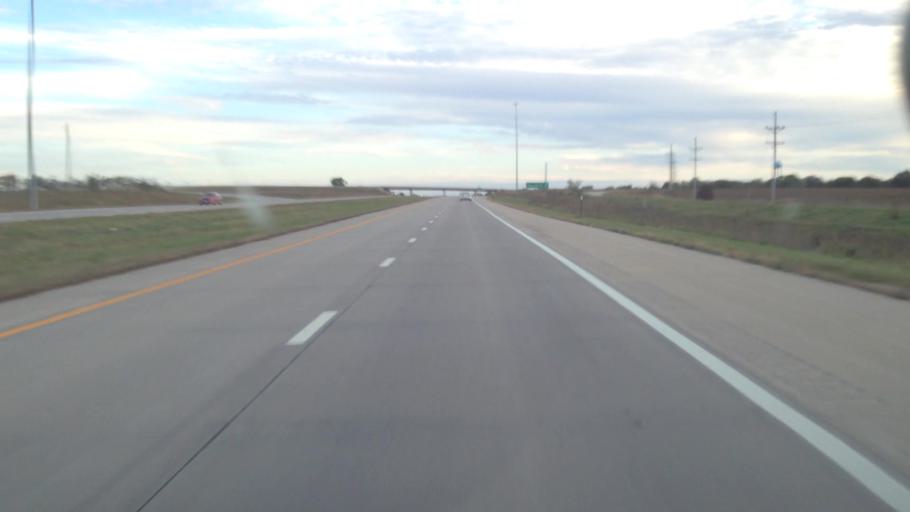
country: US
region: Kansas
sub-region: Franklin County
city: Ottawa
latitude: 38.6941
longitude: -95.2678
